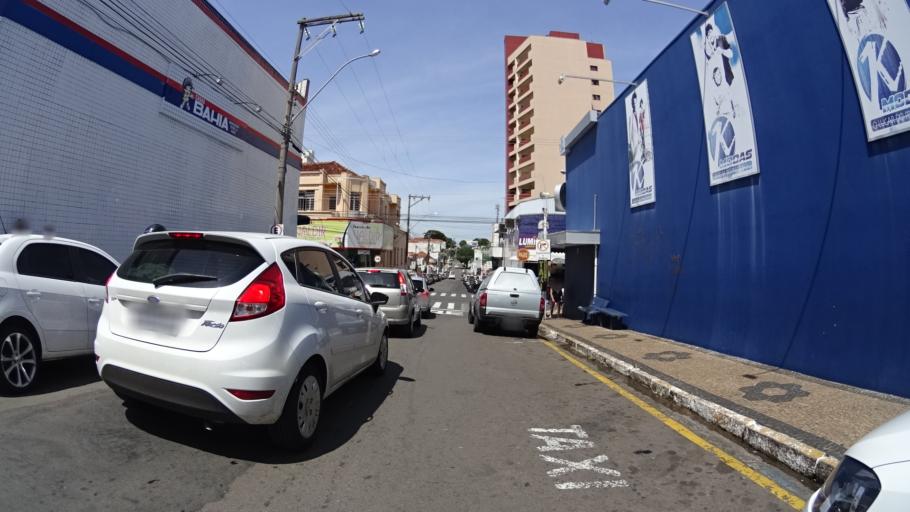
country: BR
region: Sao Paulo
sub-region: Marilia
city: Marilia
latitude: -22.2163
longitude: -49.9506
